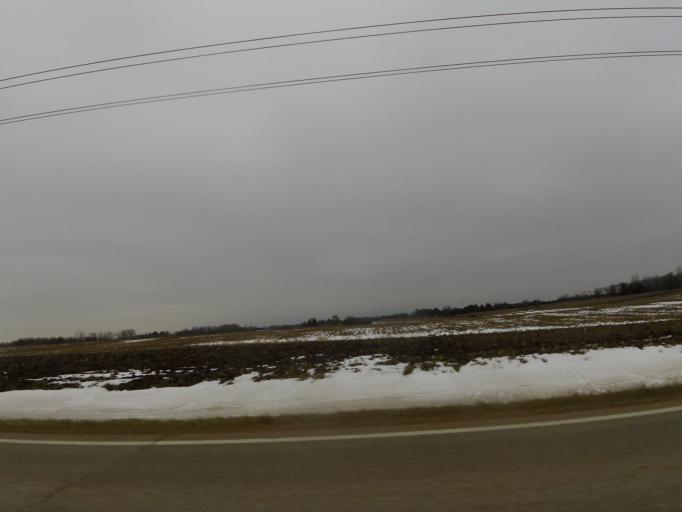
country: US
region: Minnesota
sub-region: Carver County
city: Carver
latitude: 44.7180
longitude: -93.6572
